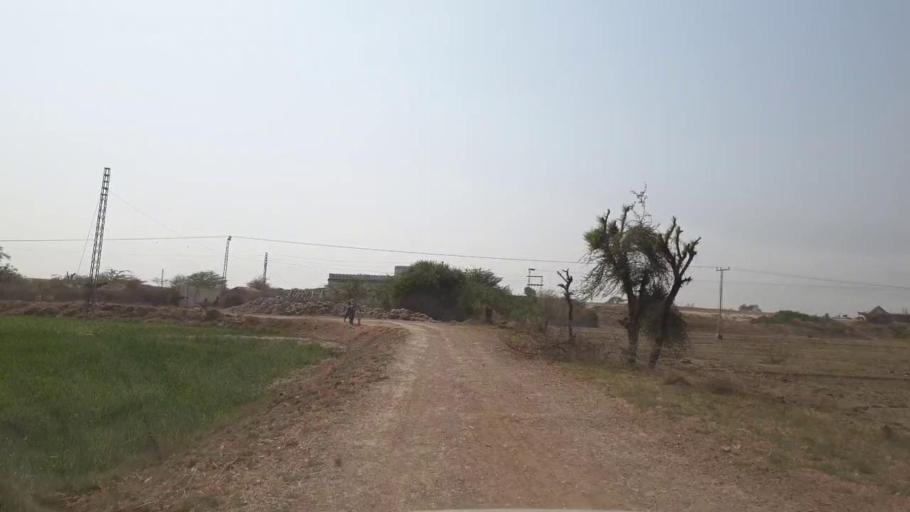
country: PK
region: Sindh
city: Mirpur Khas
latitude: 25.6435
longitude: 69.1521
